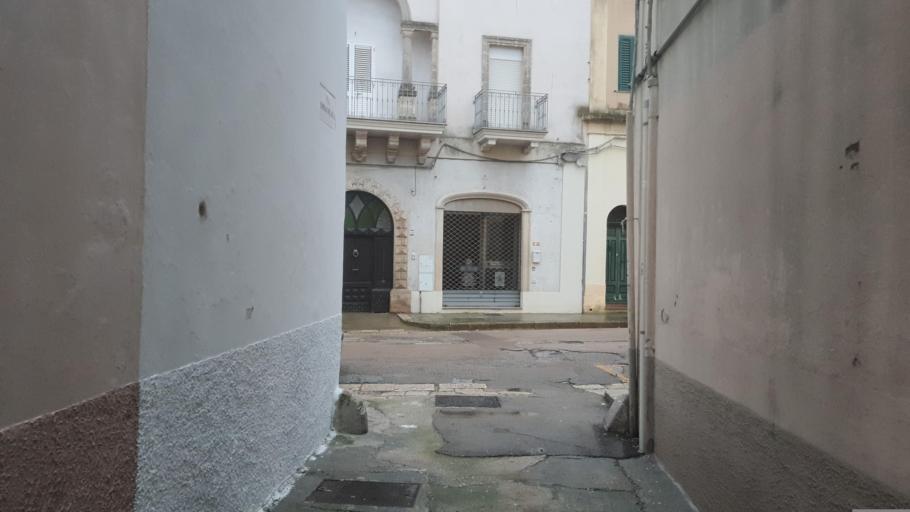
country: IT
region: Apulia
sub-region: Provincia di Lecce
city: Tricase
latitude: 39.9298
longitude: 18.3603
